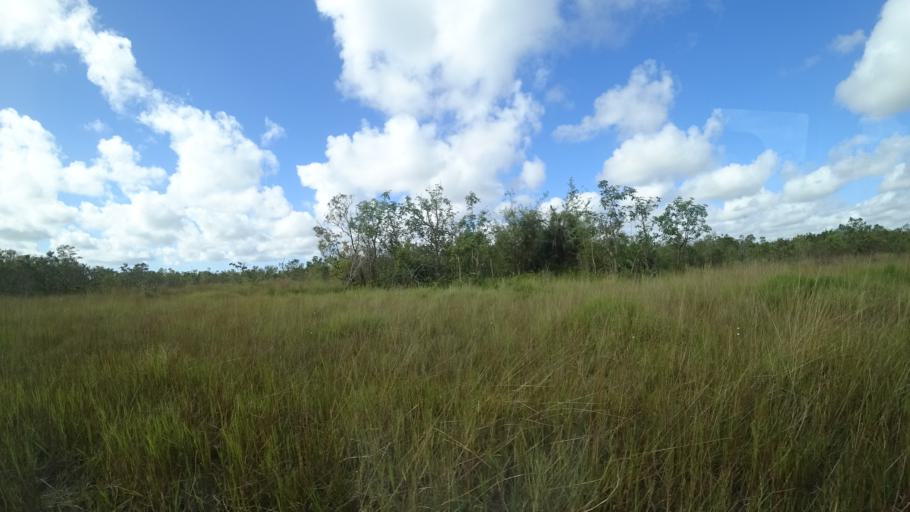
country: MZ
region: Sofala
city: Beira
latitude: -19.6162
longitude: 35.0625
